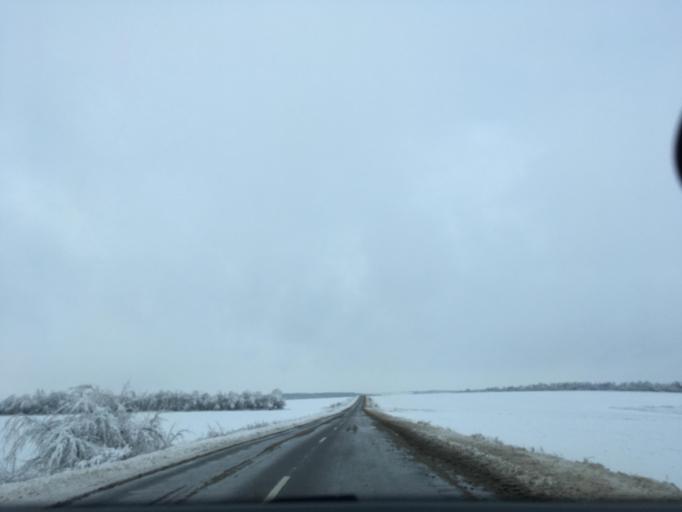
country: RU
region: Voronezj
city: Ol'khovatka
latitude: 50.1358
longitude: 39.2003
